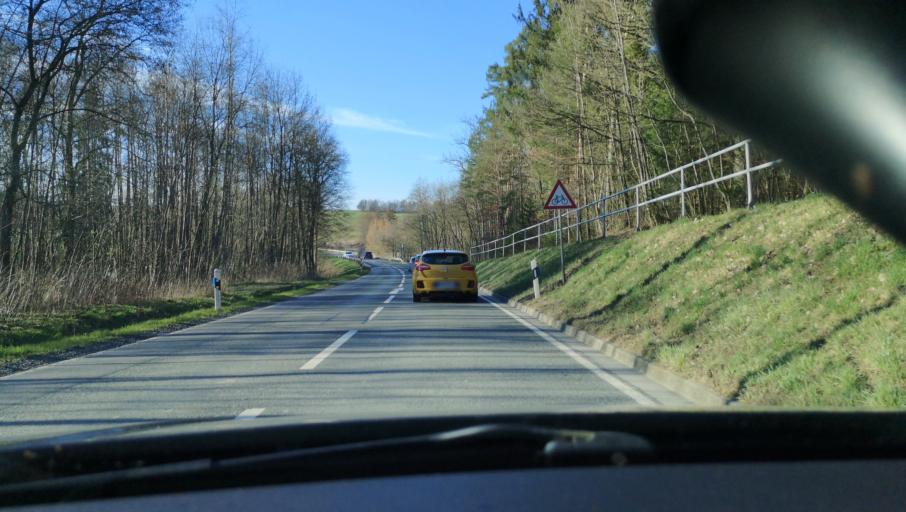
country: DE
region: Bavaria
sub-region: Upper Franconia
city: Sonnefeld
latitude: 50.2359
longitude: 11.1217
